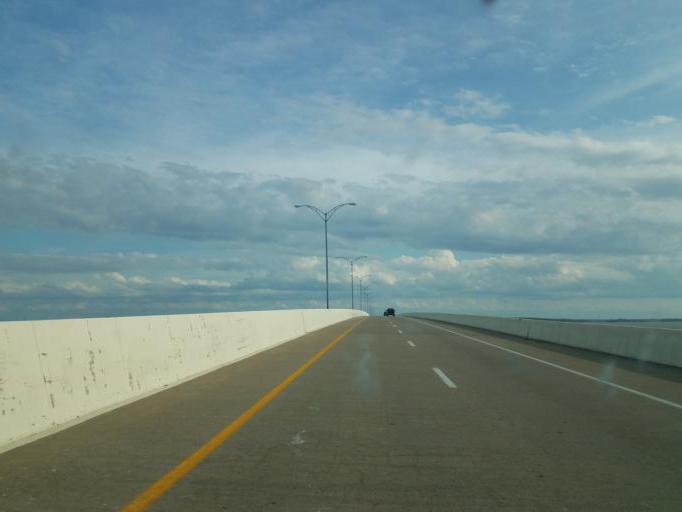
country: US
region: Ohio
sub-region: Ottawa County
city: Port Clinton
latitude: 41.4835
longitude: -82.8348
